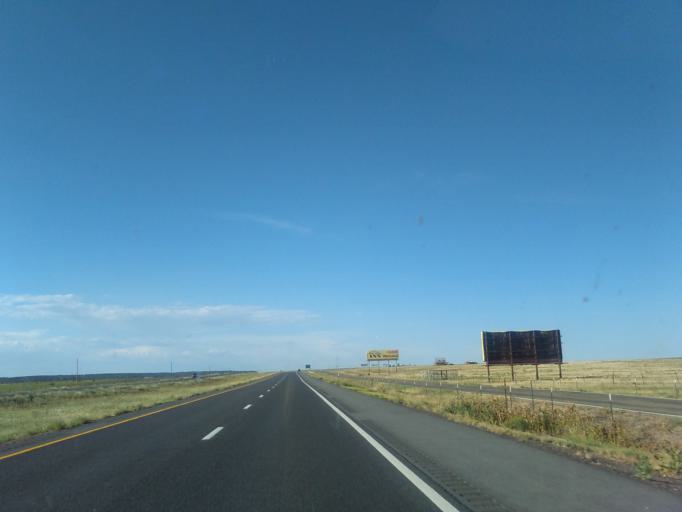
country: US
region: New Mexico
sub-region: San Miguel County
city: Las Vegas
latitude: 35.6596
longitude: -105.1875
